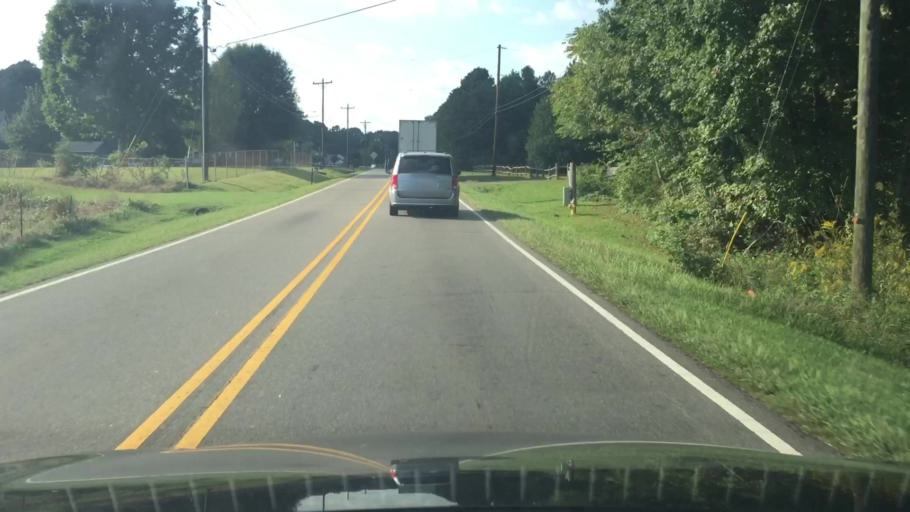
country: US
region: North Carolina
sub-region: Iredell County
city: Mooresville
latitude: 35.6157
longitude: -80.8212
